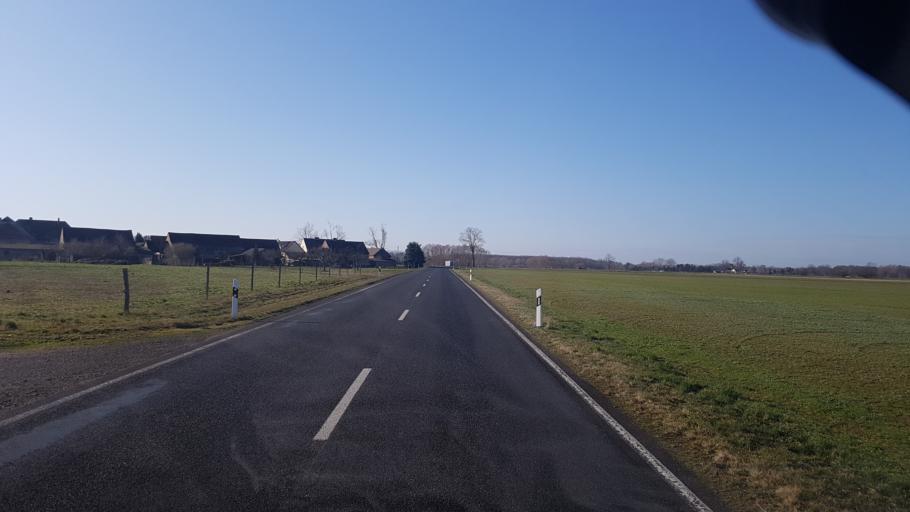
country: DE
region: Brandenburg
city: Luebben
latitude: 51.8548
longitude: 13.8446
